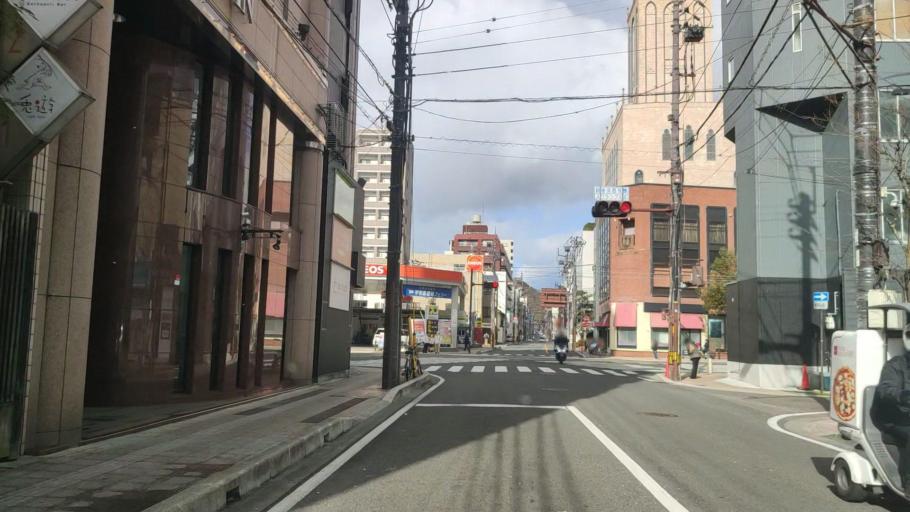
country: JP
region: Ehime
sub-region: Shikoku-chuo Shi
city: Matsuyama
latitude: 33.8410
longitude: 132.7723
